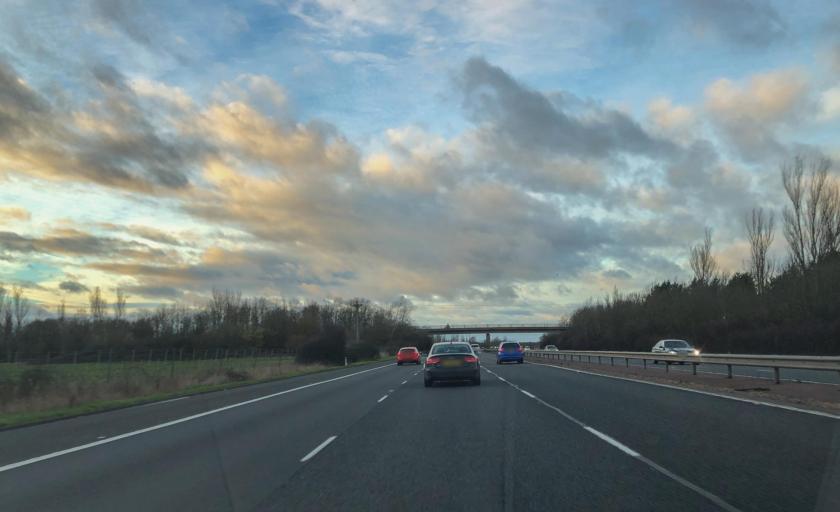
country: GB
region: England
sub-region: Oxfordshire
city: Bicester
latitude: 51.8319
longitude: -1.1221
